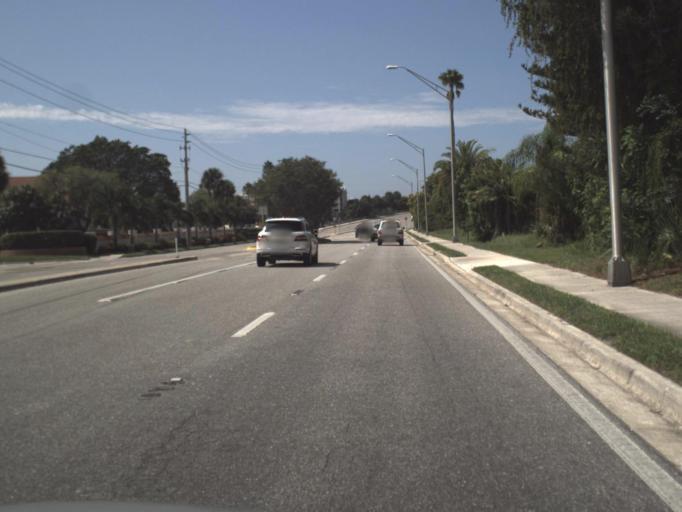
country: US
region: Florida
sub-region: Sarasota County
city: Gulf Gate Estates
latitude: 27.2566
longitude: -82.5279
